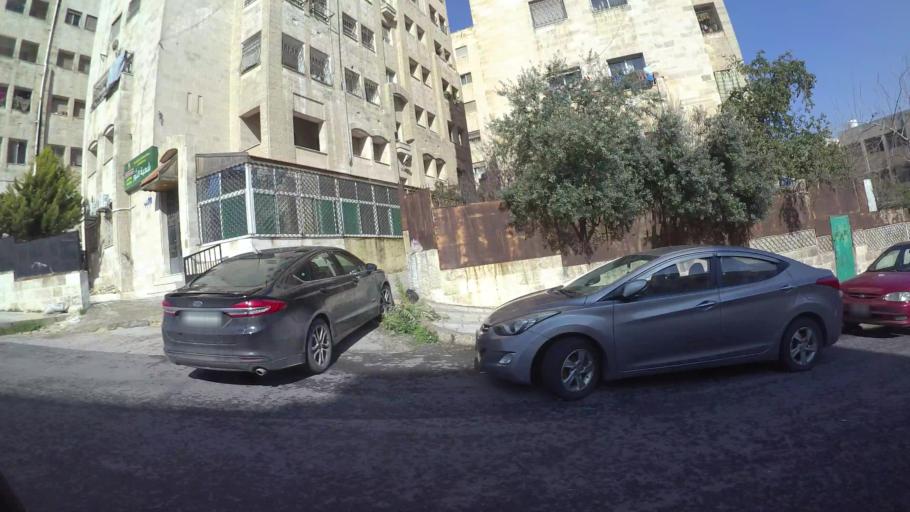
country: JO
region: Amman
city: Al Bunayyat ash Shamaliyah
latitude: 31.9328
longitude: 35.9079
